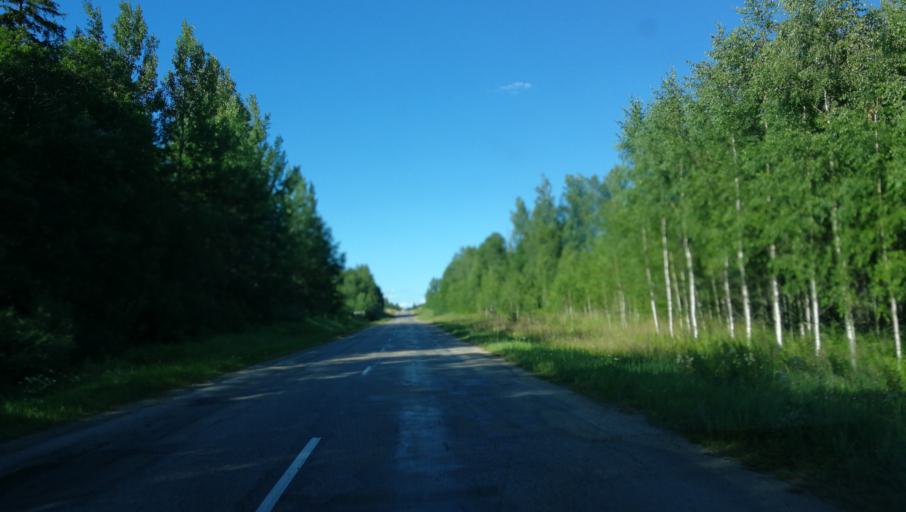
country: LV
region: Madonas Rajons
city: Madona
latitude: 56.9559
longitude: 26.0435
